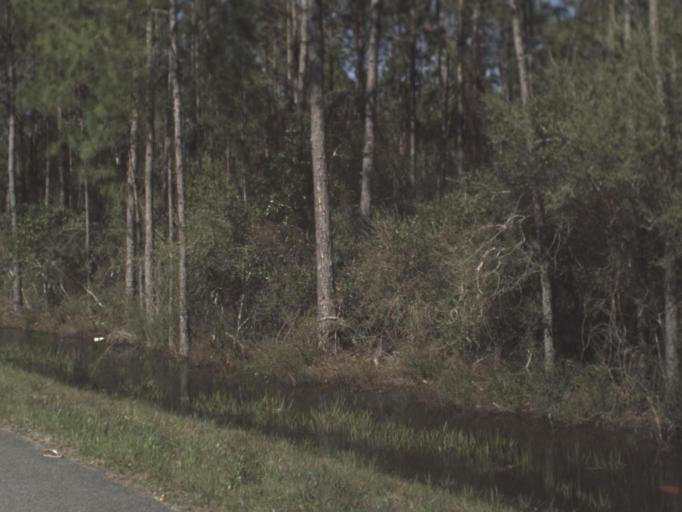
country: US
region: Florida
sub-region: Gulf County
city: Wewahitchka
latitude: 29.9853
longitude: -85.1680
